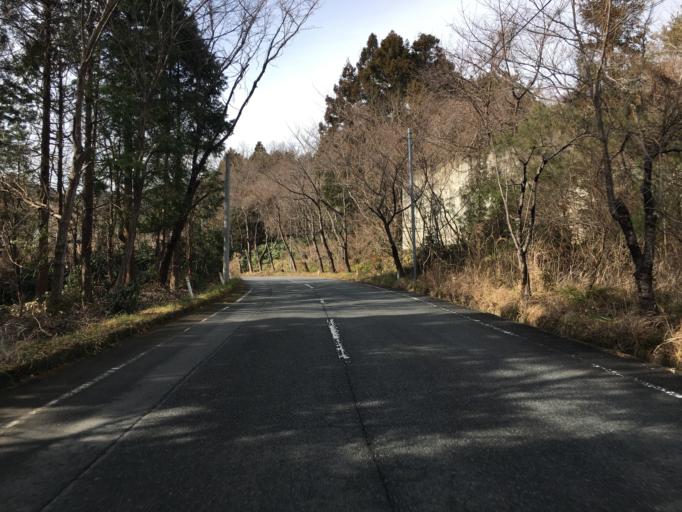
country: JP
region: Fukushima
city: Iwaki
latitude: 37.1284
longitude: 140.8406
